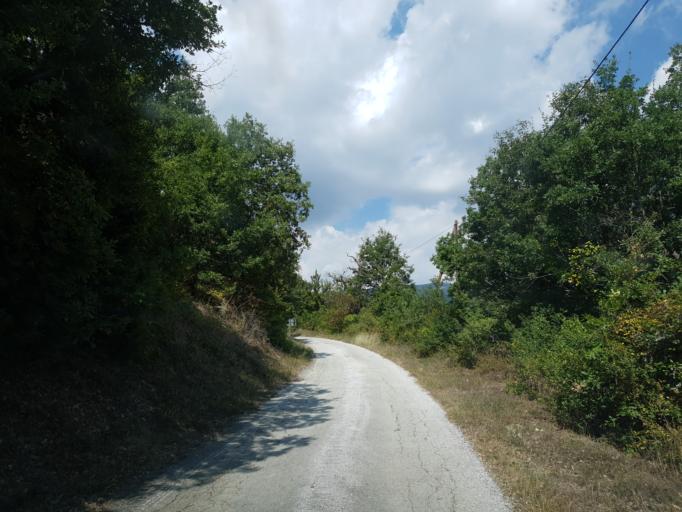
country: MK
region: Makedonski Brod
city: Samokov
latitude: 41.7443
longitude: 21.1055
